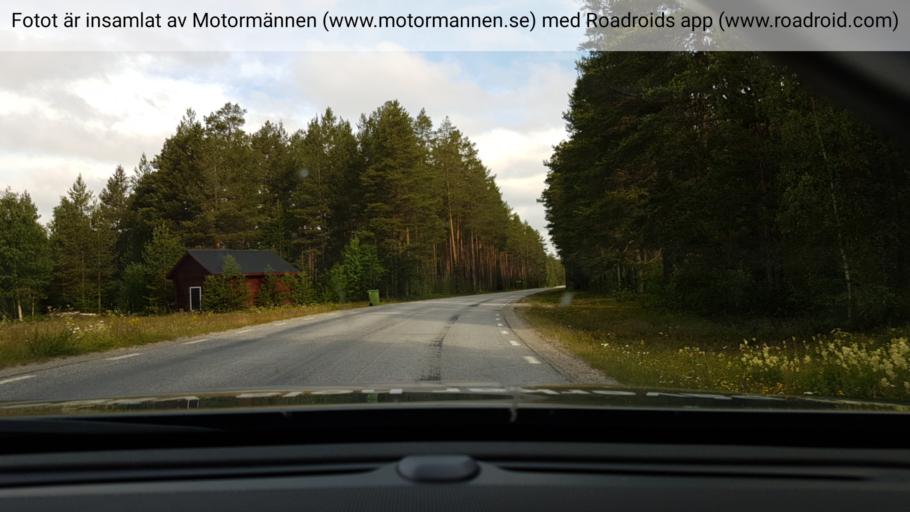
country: SE
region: Vaesterbotten
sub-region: Vindelns Kommun
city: Vindeln
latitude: 64.2790
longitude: 19.6247
